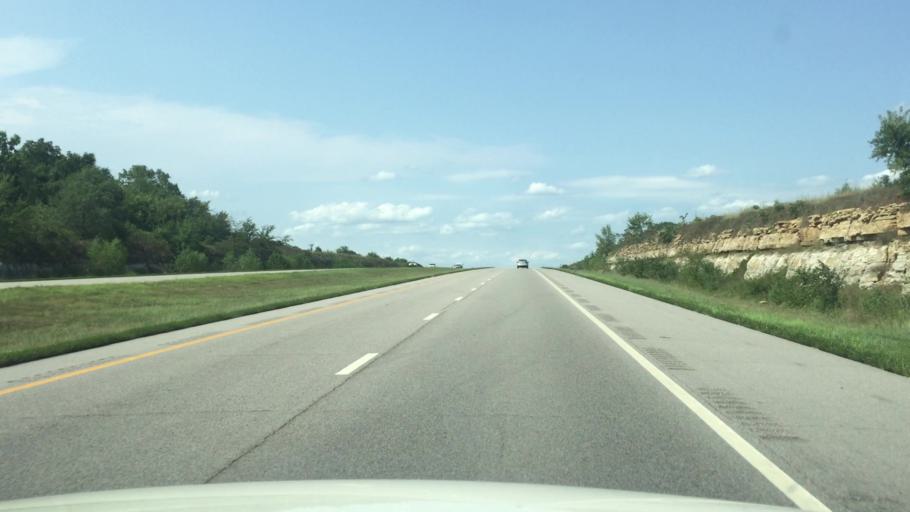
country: US
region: Kansas
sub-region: Linn County
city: La Cygne
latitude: 38.4345
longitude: -94.6867
